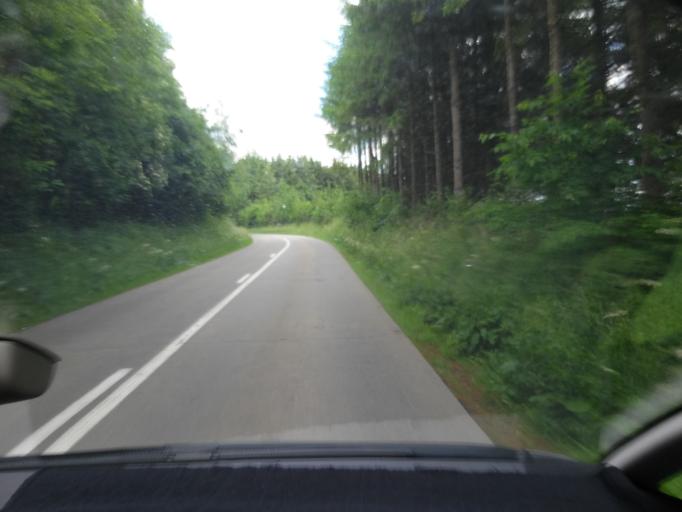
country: BE
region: Wallonia
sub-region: Province de Namur
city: Hamois
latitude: 50.2707
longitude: 5.1729
